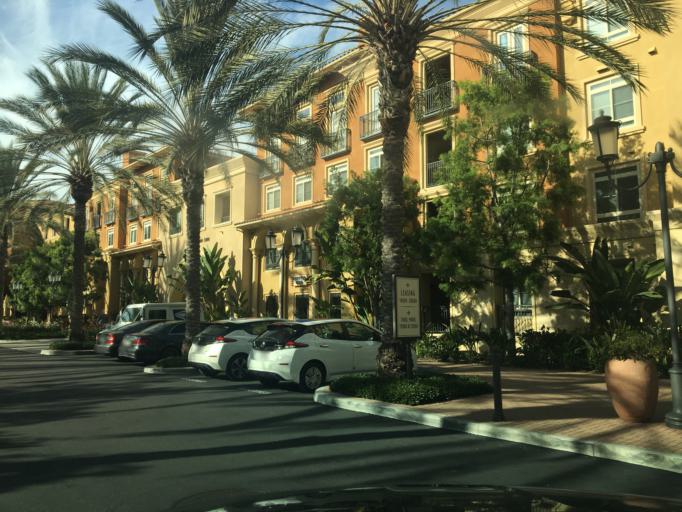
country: US
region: California
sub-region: Orange County
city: Laguna Woods
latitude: 33.6540
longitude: -117.7536
